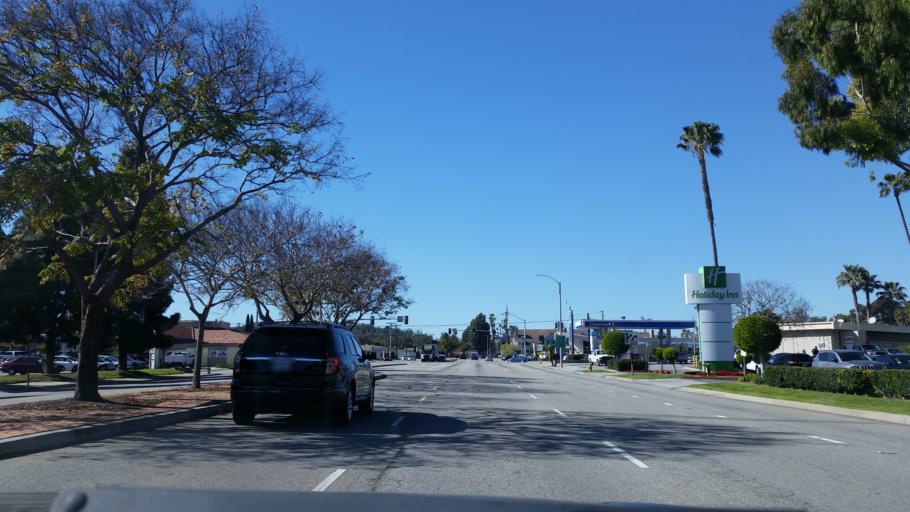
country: US
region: California
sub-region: Los Angeles County
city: Signal Hill
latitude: 33.8034
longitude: -118.1411
